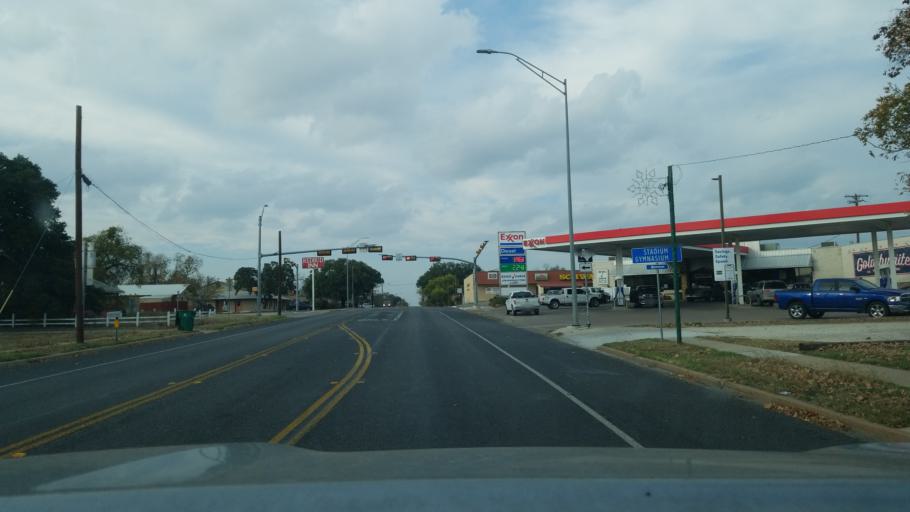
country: US
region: Texas
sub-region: Mills County
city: Goldthwaite
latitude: 31.4542
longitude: -98.5708
